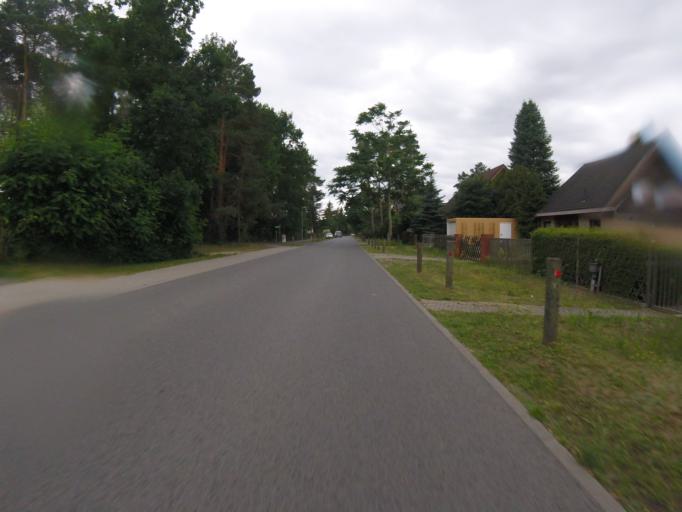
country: DE
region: Brandenburg
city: Bestensee
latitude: 52.2276
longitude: 13.6373
